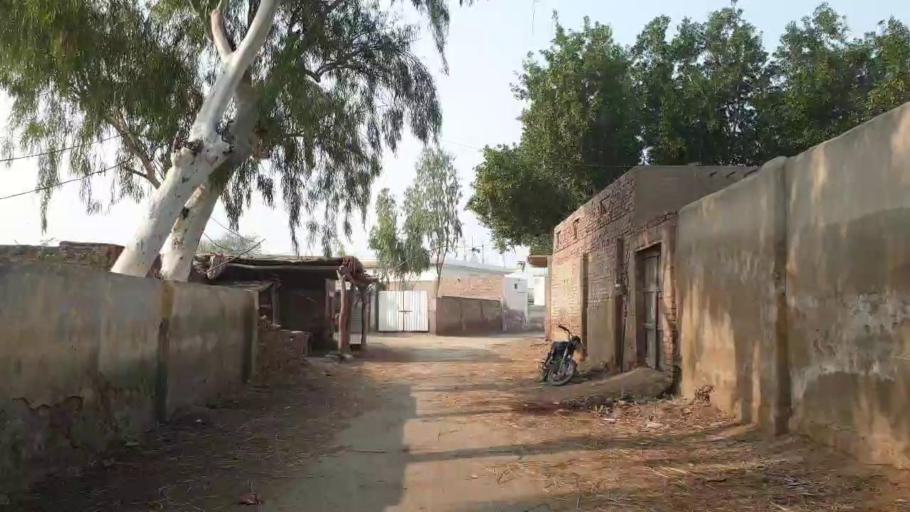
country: PK
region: Sindh
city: Tando Muhammad Khan
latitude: 25.1423
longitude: 68.6113
